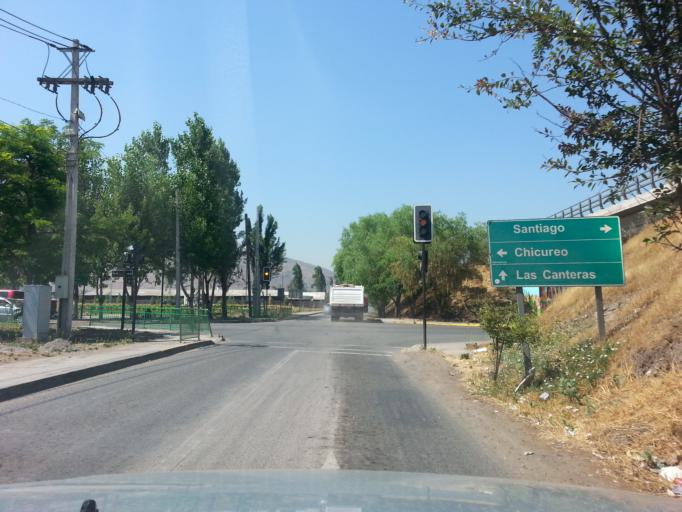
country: CL
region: Santiago Metropolitan
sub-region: Provincia de Chacabuco
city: Chicureo Abajo
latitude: -33.2851
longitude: -70.7013
